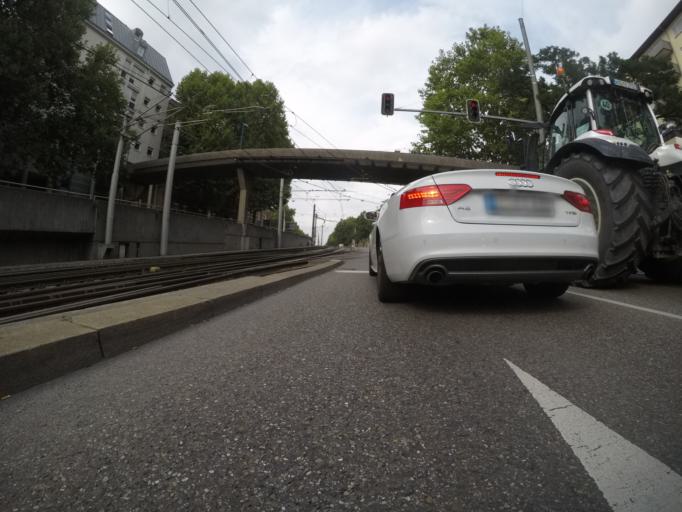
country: DE
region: Baden-Wuerttemberg
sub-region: Regierungsbezirk Stuttgart
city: Stuttgart
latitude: 48.7937
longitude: 9.1820
